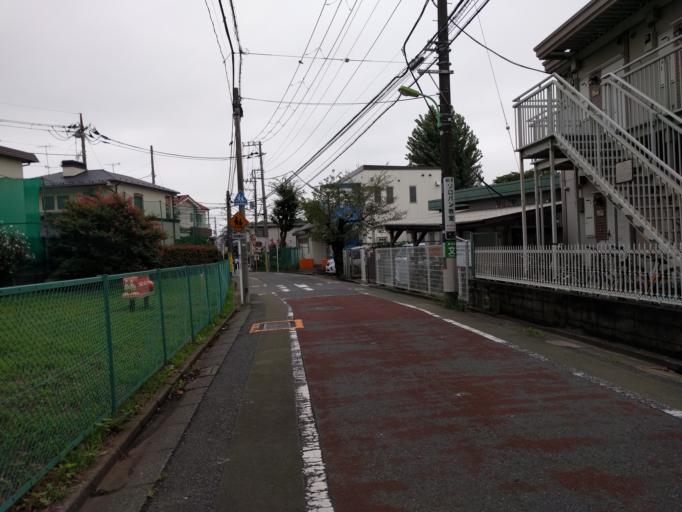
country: JP
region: Tokyo
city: Tokyo
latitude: 35.6271
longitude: 139.6527
